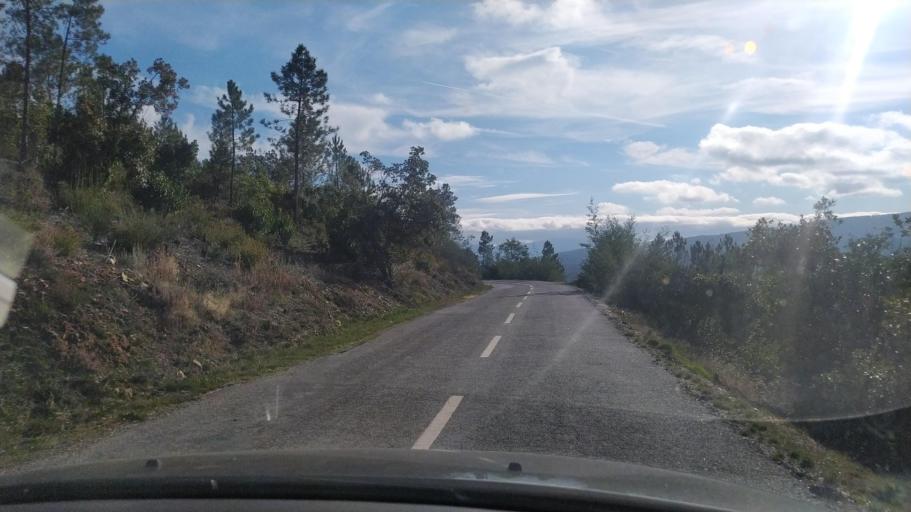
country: PT
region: Coimbra
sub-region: Oliveira do Hospital
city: Oliveira do Hospital
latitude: 40.1979
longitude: -7.7270
